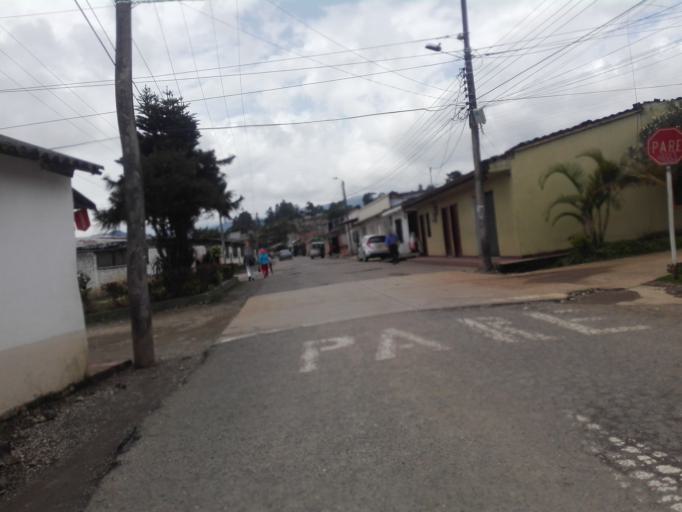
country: CO
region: Cauca
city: Popayan
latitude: 2.3513
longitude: -76.6779
